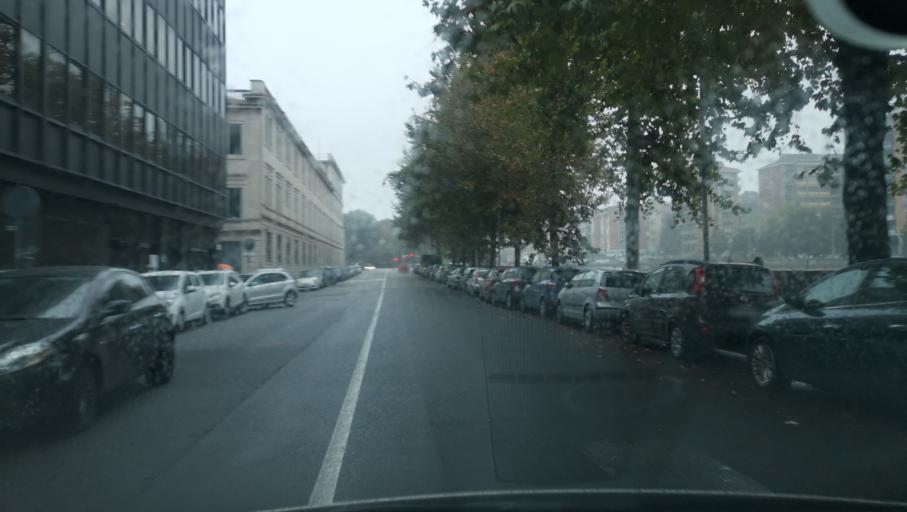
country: IT
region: Piedmont
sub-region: Provincia di Torino
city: Turin
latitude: 45.0773
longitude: 7.6913
